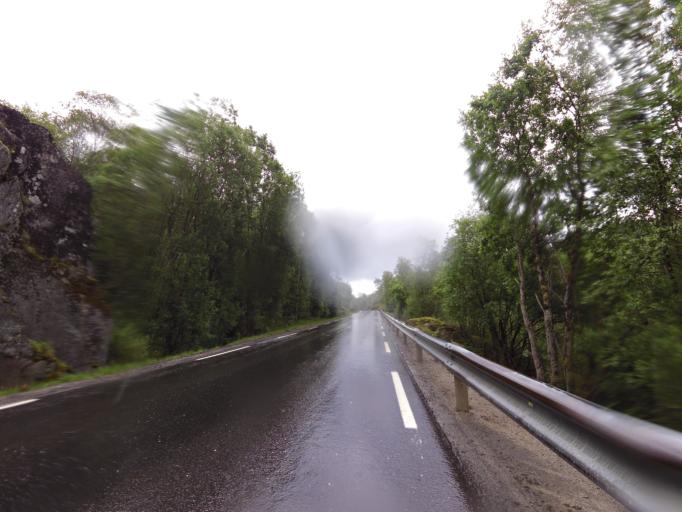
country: NO
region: Vest-Agder
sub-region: Lyngdal
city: Lyngdal
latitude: 58.1102
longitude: 7.0880
